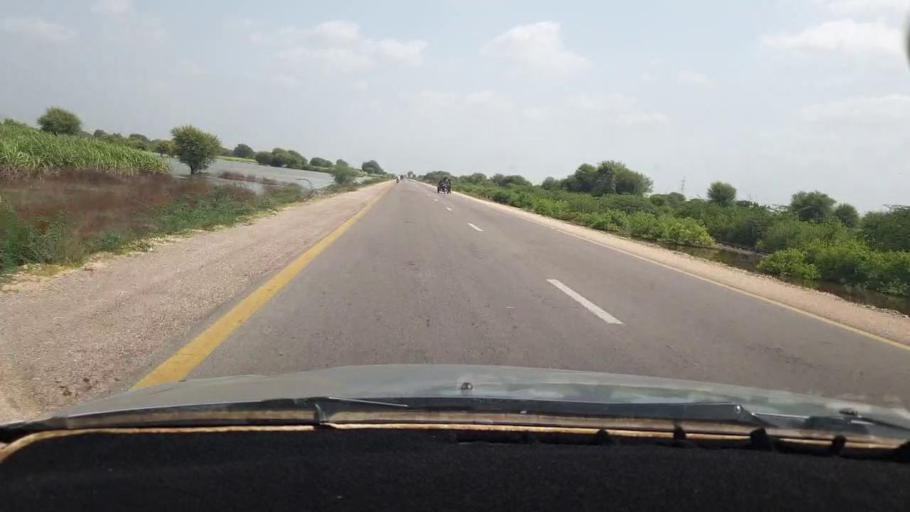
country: PK
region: Sindh
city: Digri
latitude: 25.1075
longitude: 69.1650
